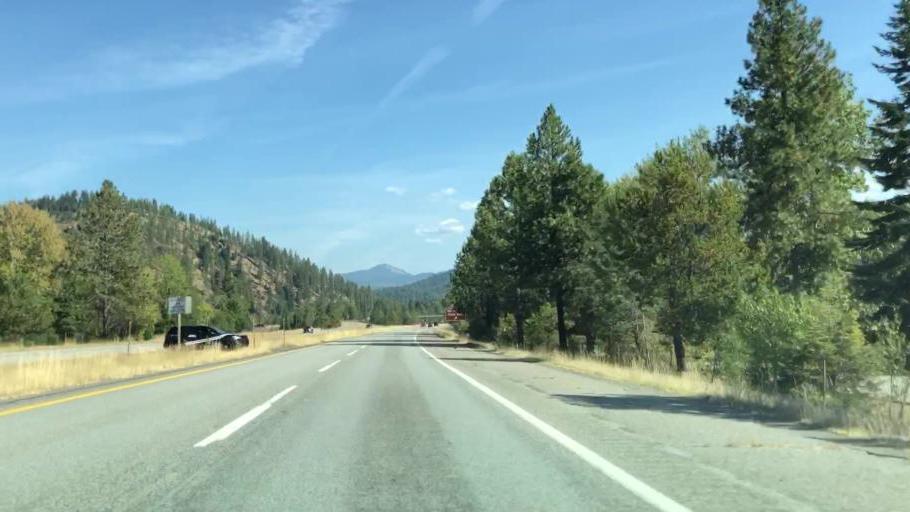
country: US
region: Idaho
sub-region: Shoshone County
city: Pinehurst
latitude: 47.5524
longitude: -116.3605
